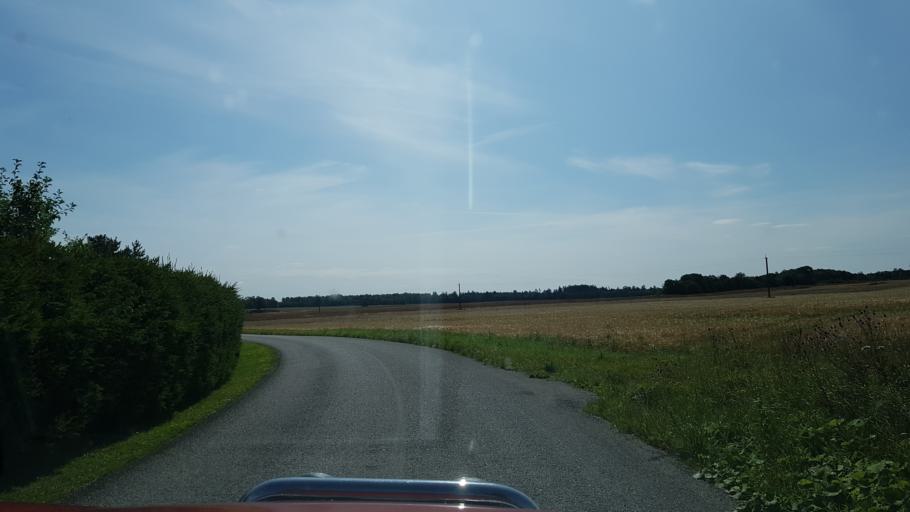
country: EE
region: Jaervamaa
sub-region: Jaerva-Jaani vald
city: Jarva-Jaani
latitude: 59.0855
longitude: 25.7531
